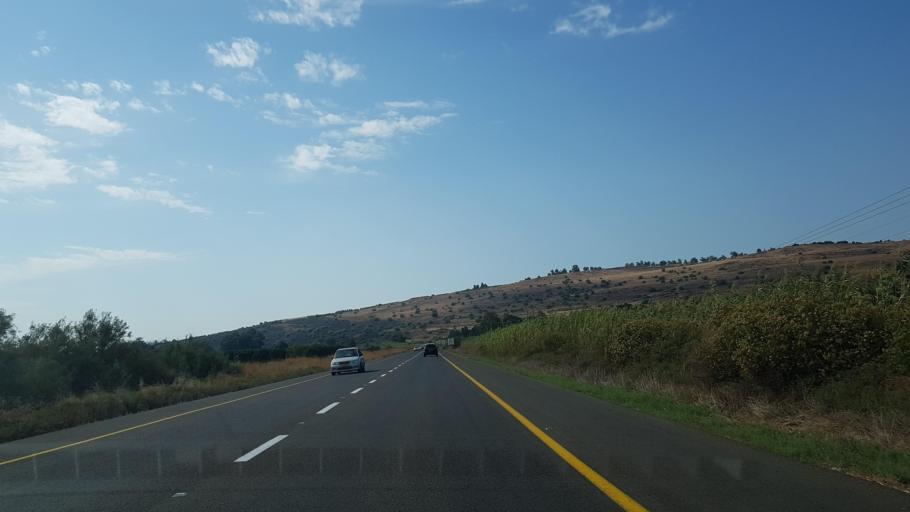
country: SY
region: Quneitra
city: Al Butayhah
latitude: 32.9043
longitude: 35.6263
